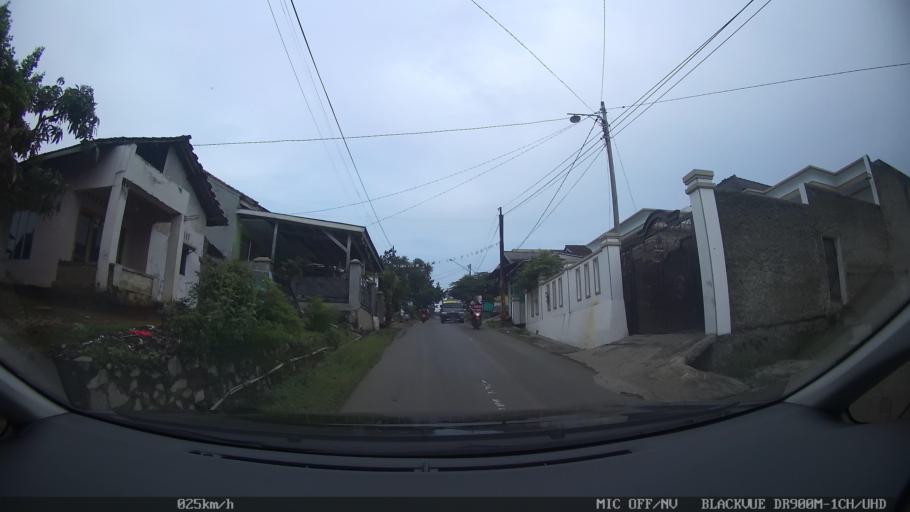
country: ID
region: Lampung
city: Bandarlampung
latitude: -5.4041
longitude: 105.2371
